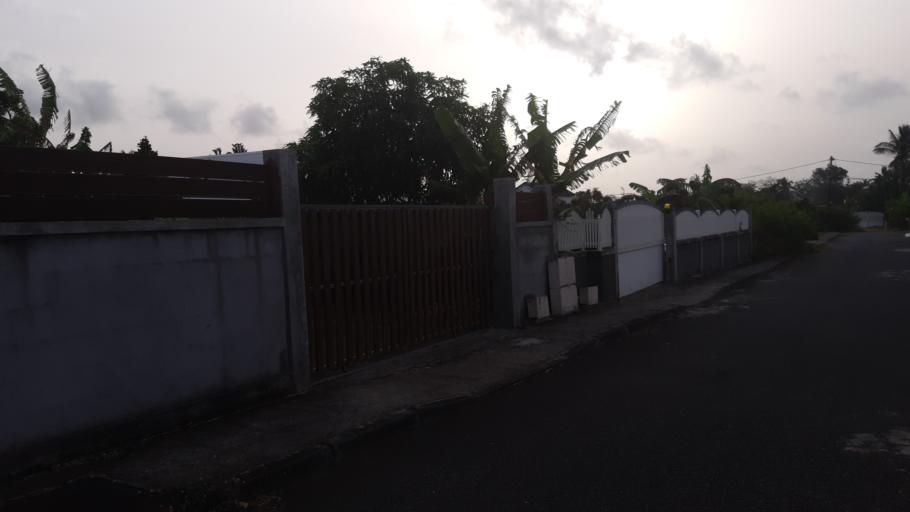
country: GP
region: Guadeloupe
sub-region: Guadeloupe
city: Petit-Canal
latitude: 16.4070
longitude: -61.4200
